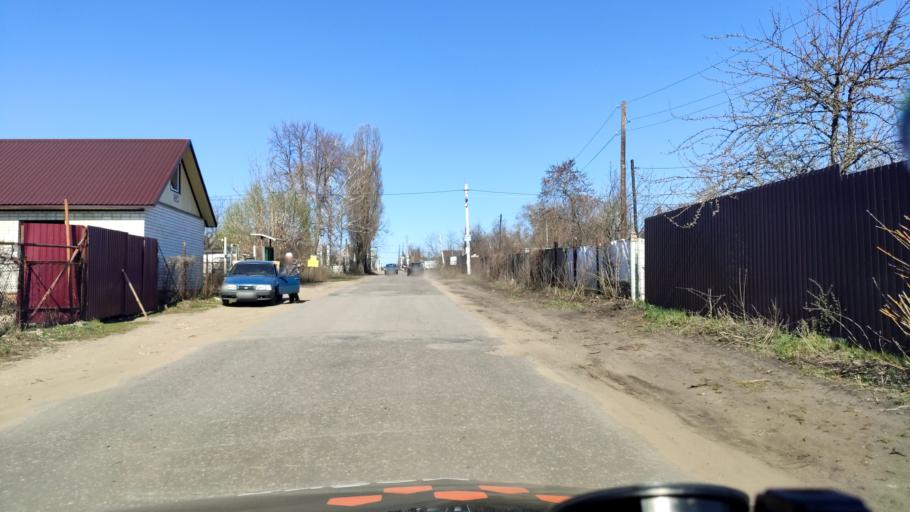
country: RU
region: Voronezj
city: Shilovo
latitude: 51.5970
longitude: 39.1494
